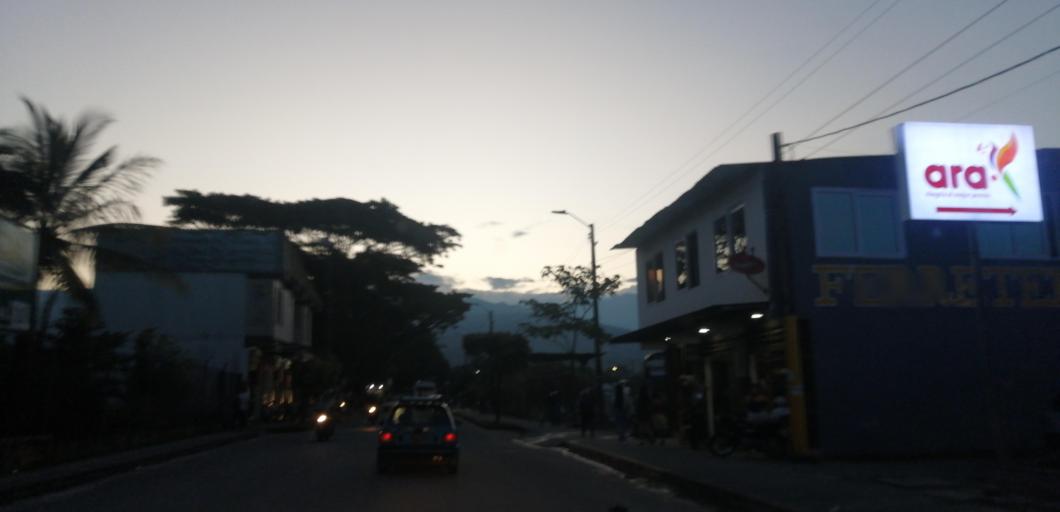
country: CO
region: Meta
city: Acacias
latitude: 3.9885
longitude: -73.7770
